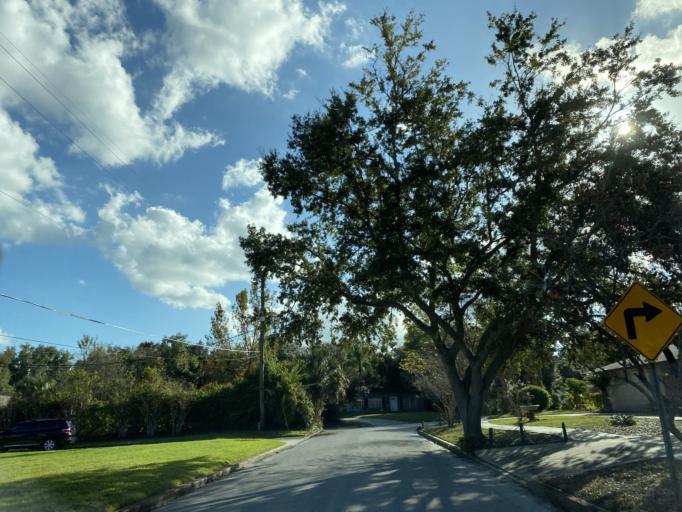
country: US
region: Florida
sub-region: Orange County
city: Orlando
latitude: 28.5482
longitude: -81.4036
